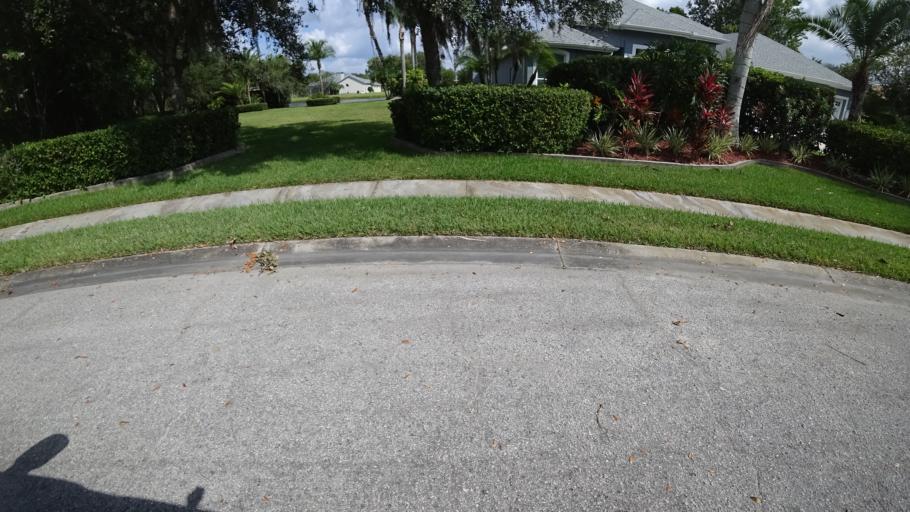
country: US
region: Florida
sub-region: Sarasota County
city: The Meadows
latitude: 27.4057
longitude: -82.4353
